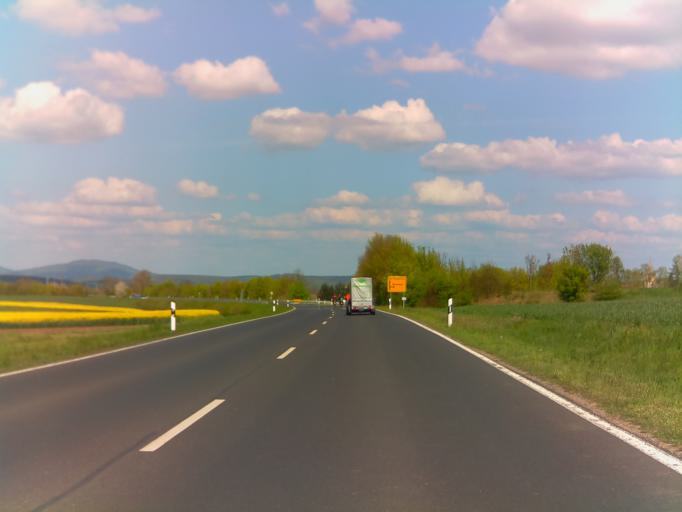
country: DE
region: Bavaria
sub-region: Regierungsbezirk Unterfranken
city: Grosseibstadt
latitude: 50.2837
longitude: 10.4353
